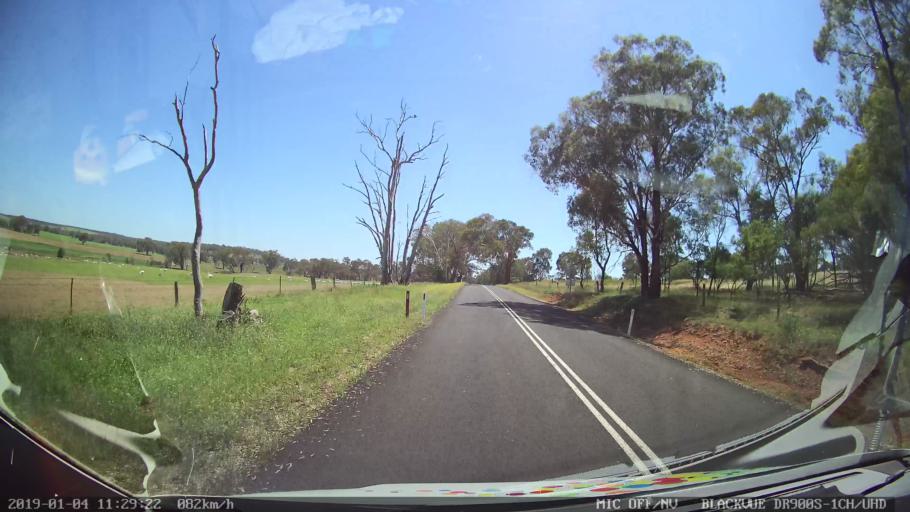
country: AU
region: New South Wales
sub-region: Cabonne
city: Molong
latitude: -33.0887
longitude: 148.7735
